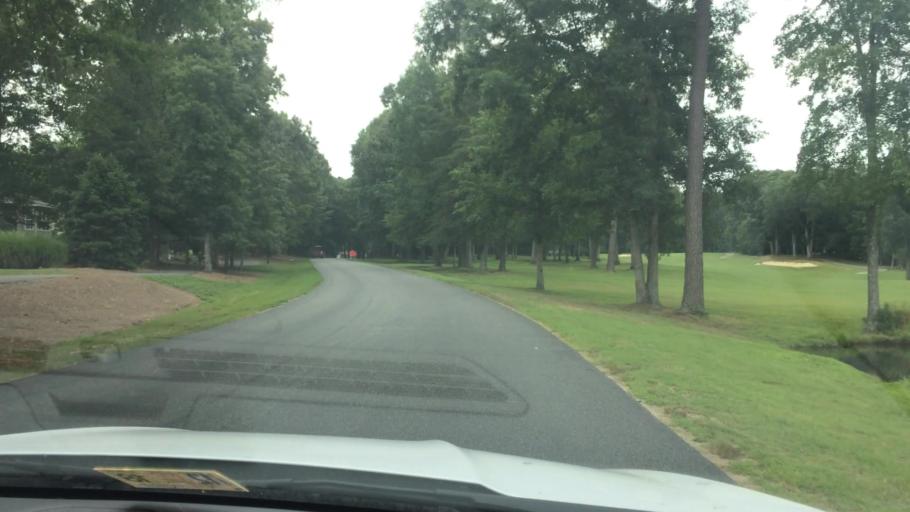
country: US
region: Virginia
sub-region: James City County
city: Williamsburg
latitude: 37.2991
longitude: -76.7955
